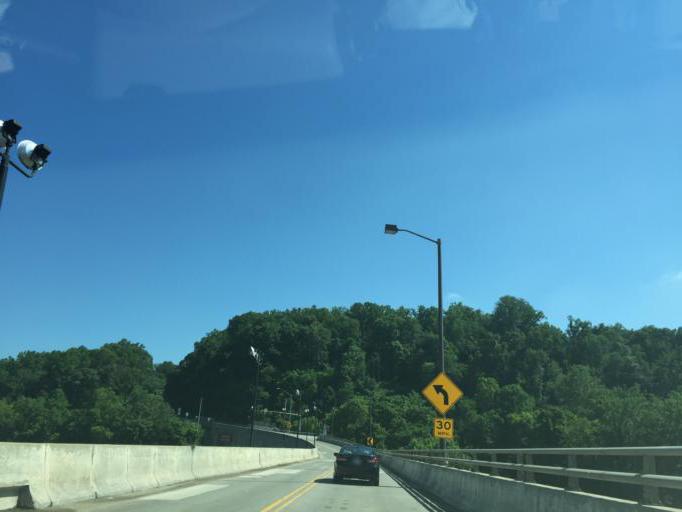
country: US
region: Maryland
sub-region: Cecil County
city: Rising Sun
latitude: 39.6661
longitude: -76.1706
